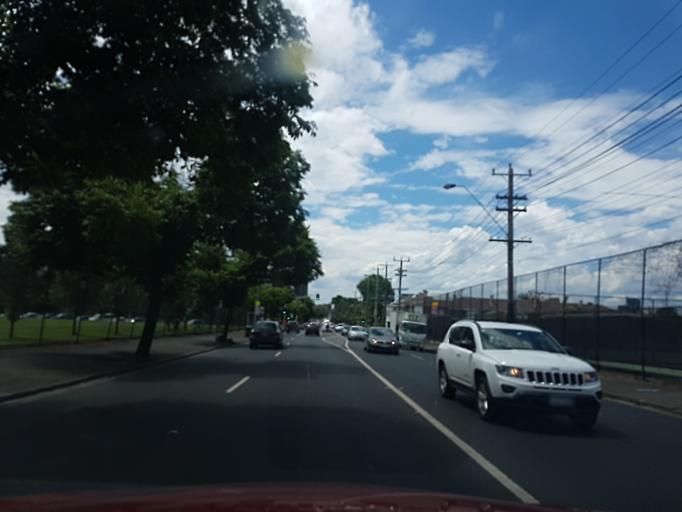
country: AU
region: Victoria
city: Windsor
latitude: -37.8493
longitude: 144.9845
